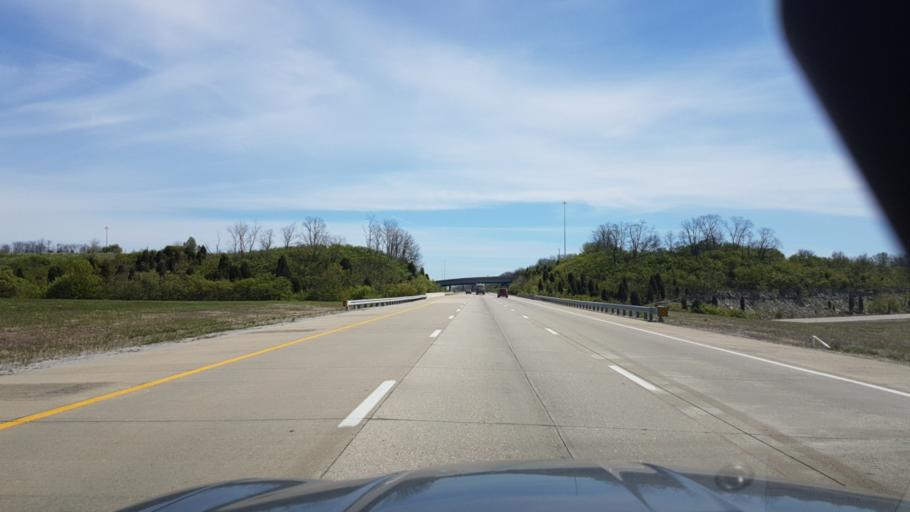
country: US
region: Kentucky
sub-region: Campbell County
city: Highland Heights
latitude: 39.0454
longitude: -84.4628
